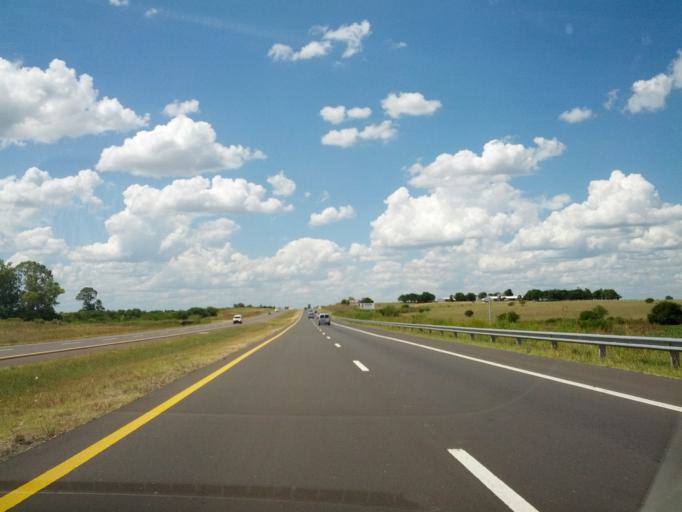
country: AR
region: Entre Rios
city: Colonia Elia
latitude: -32.5646
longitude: -58.3723
